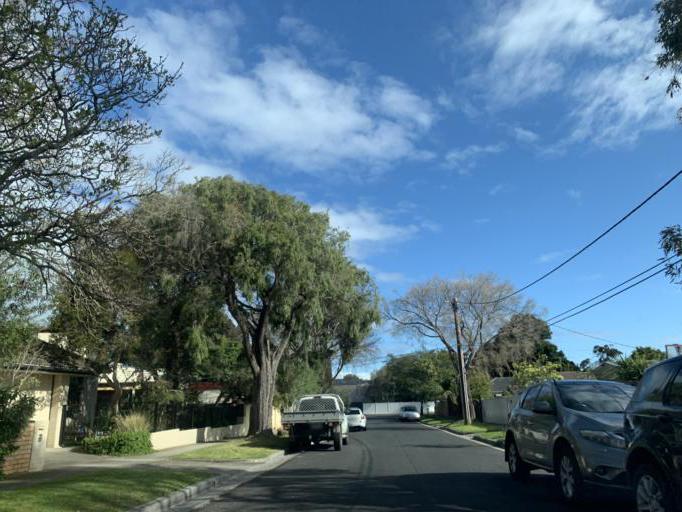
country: AU
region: Victoria
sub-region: Bayside
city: Cheltenham
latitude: -37.9730
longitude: 145.0510
